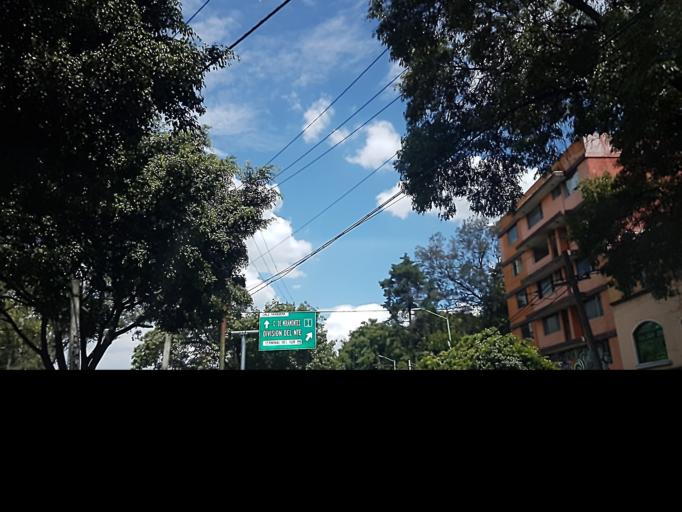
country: MX
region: Mexico City
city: Coyoacan
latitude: 19.3416
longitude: -99.1414
